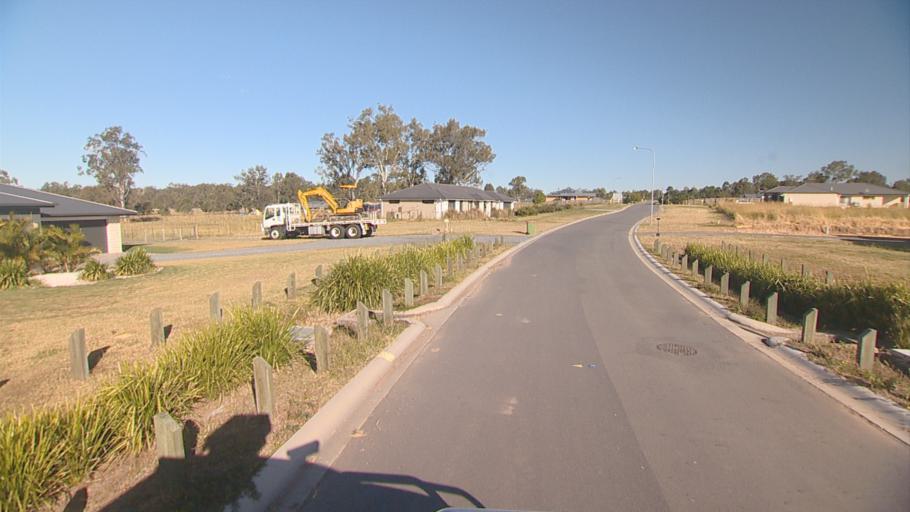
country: AU
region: Queensland
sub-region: Logan
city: North Maclean
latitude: -27.7843
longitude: 153.0257
